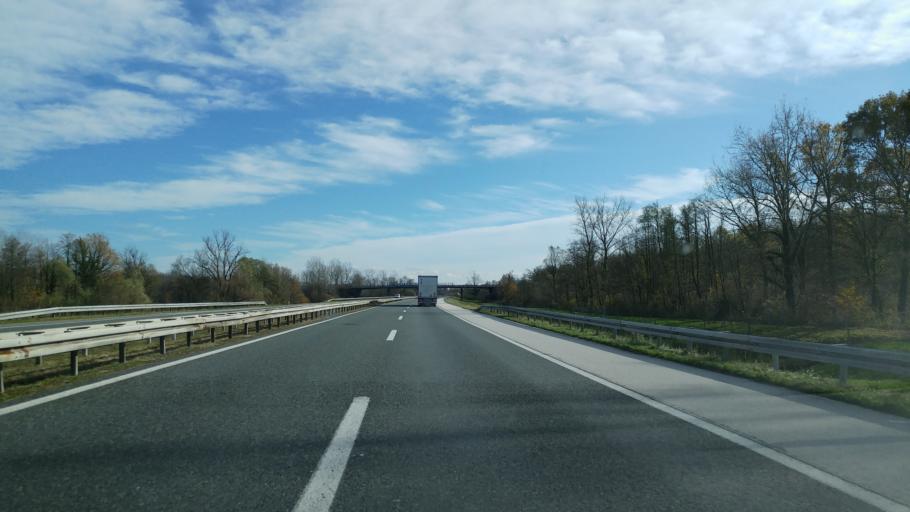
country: HR
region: Sisacko-Moslavacka
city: Husain
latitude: 45.4449
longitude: 16.8152
